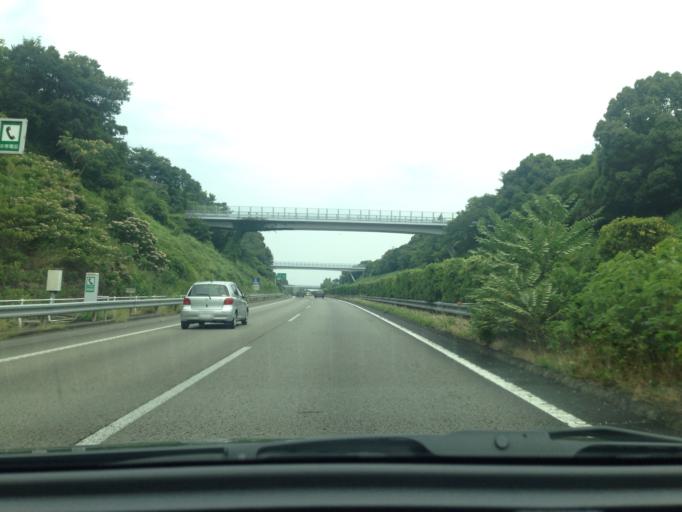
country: JP
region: Shizuoka
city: Shimada
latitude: 34.7783
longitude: 138.2291
